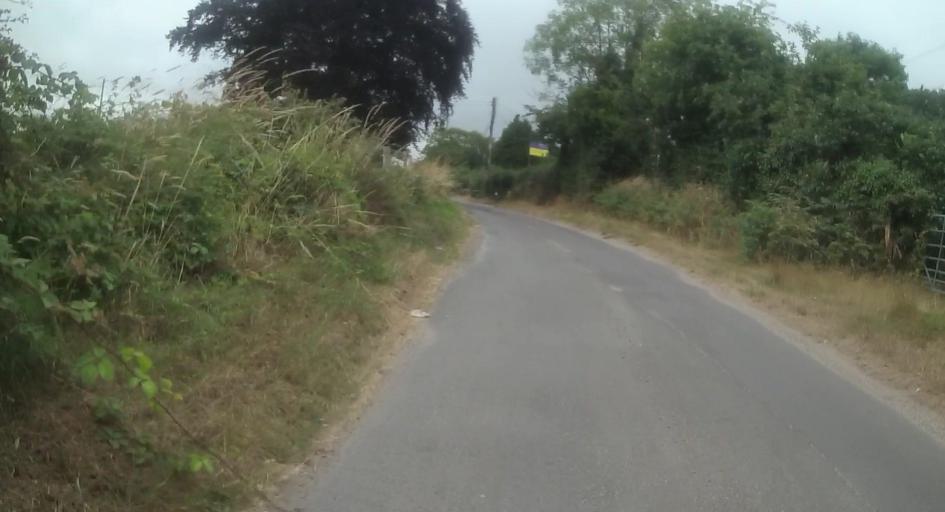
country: GB
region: England
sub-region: Dorset
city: Bovington Camp
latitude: 50.7248
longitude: -2.1944
